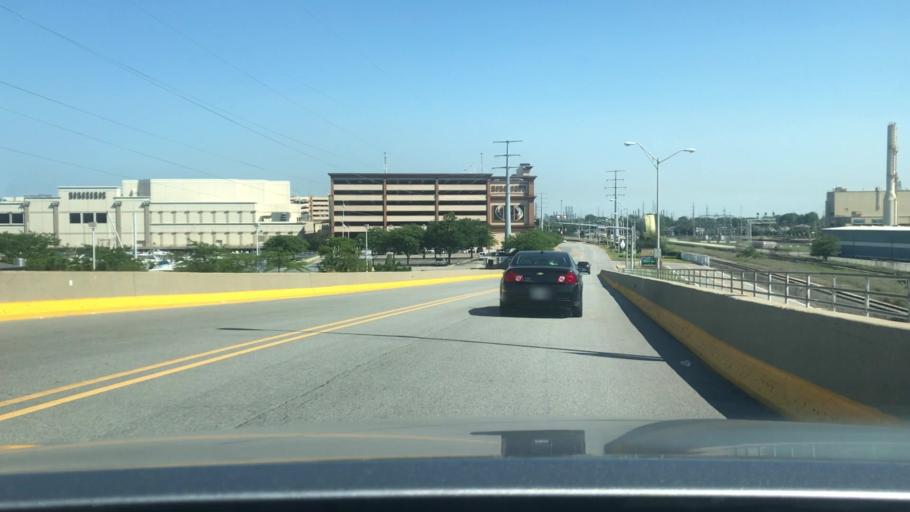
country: US
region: Indiana
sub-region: Lake County
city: Whiting
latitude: 41.6961
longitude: -87.5118
